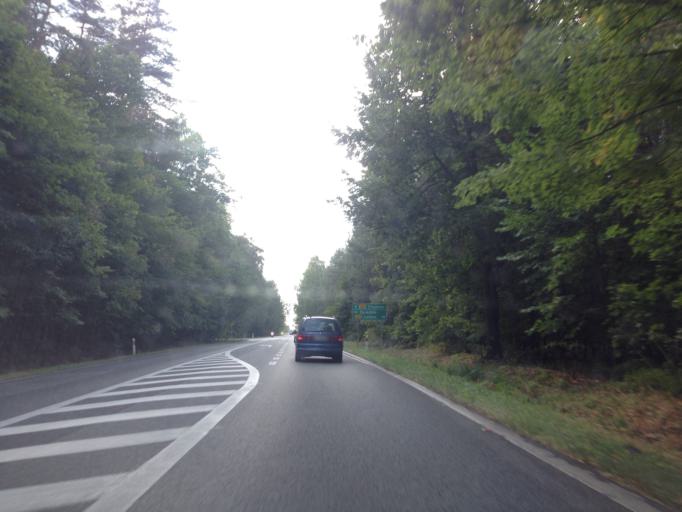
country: PL
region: Kujawsko-Pomorskie
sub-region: Powiat swiecki
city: Swiekatowo
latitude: 53.4745
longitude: 18.1538
